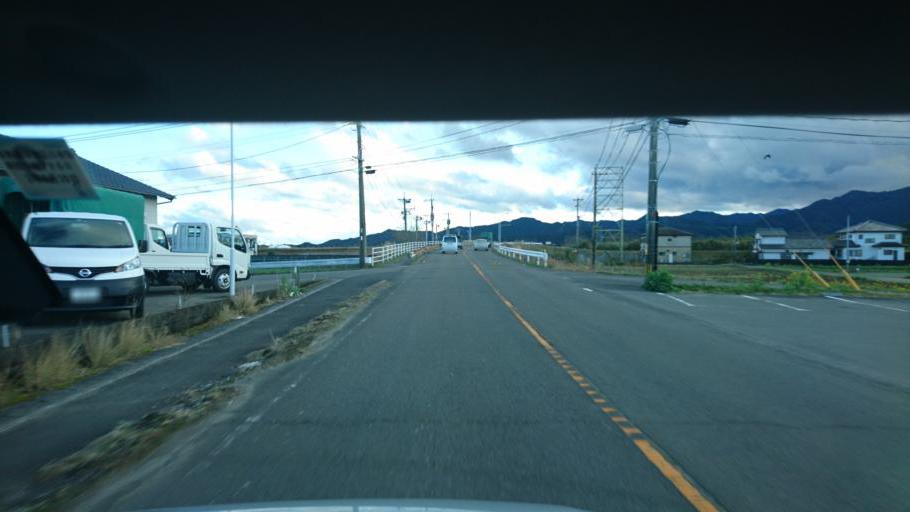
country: JP
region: Miyazaki
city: Miyazaki-shi
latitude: 31.8378
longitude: 131.4376
